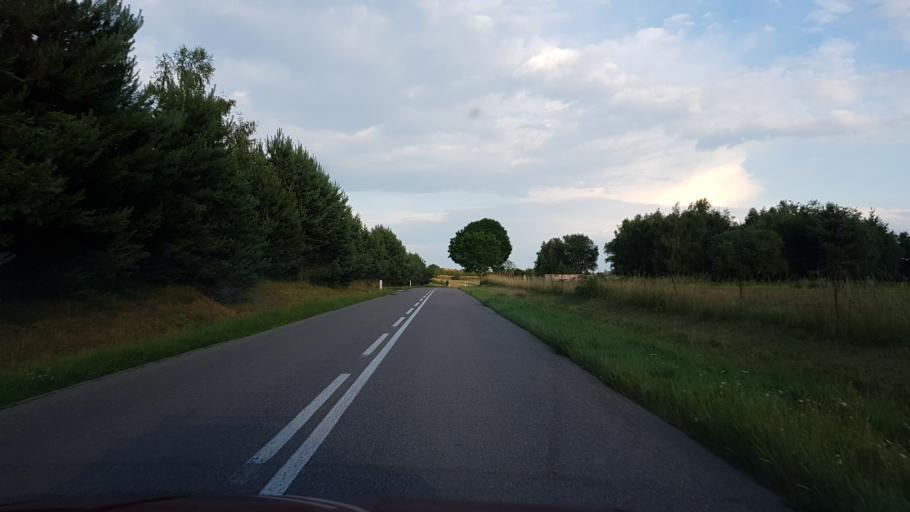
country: PL
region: West Pomeranian Voivodeship
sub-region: Powiat goleniowski
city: Nowogard
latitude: 53.6929
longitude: 15.0678
